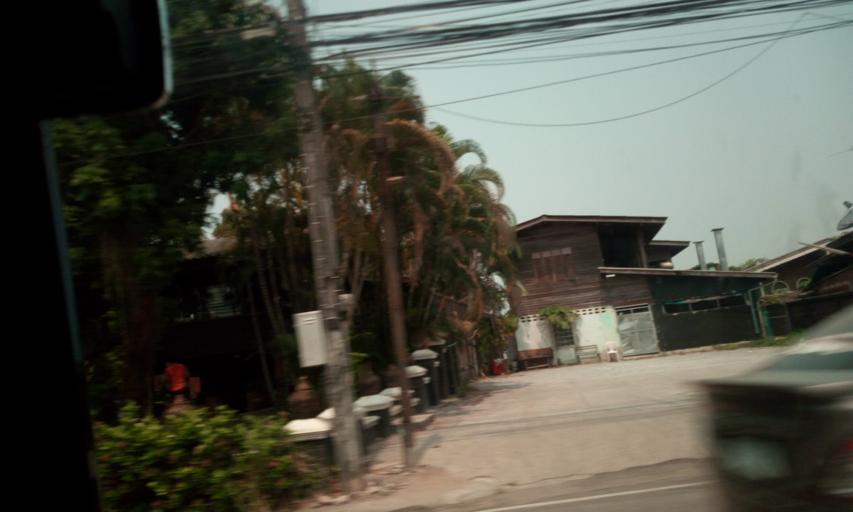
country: TH
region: Chiang Rai
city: Chiang Rai
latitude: 19.8849
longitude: 99.8307
